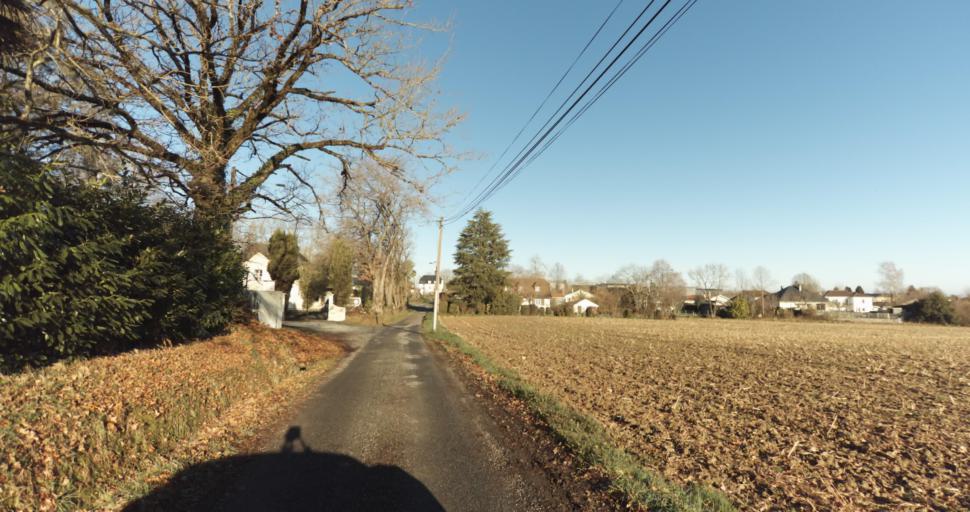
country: FR
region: Aquitaine
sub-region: Departement des Pyrenees-Atlantiques
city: Morlaas
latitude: 43.3389
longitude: -0.2626
